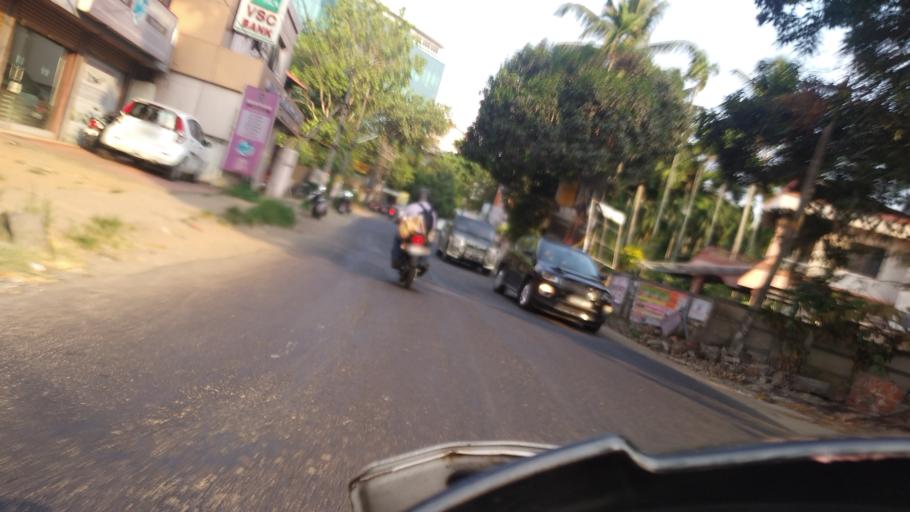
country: IN
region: Kerala
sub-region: Thrissur District
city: Thanniyam
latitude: 10.3995
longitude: 76.1135
